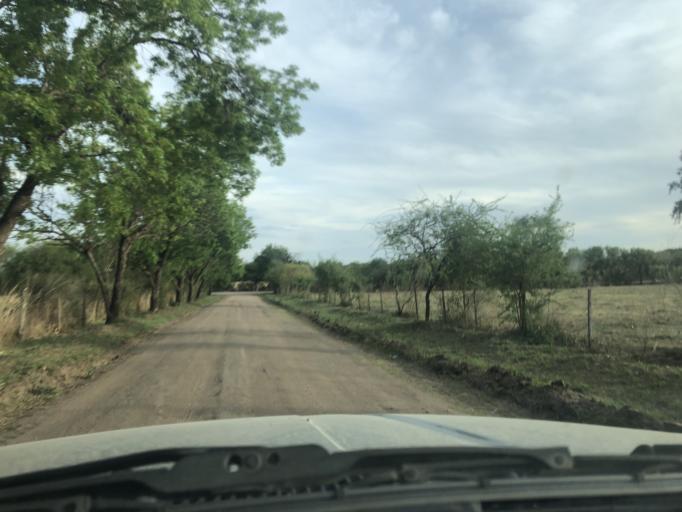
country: AR
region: Cordoba
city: La Granja
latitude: -31.0164
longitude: -64.2515
